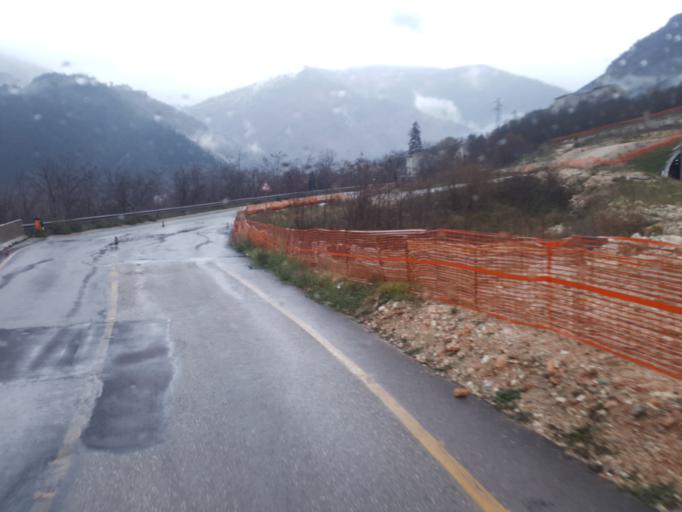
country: IT
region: The Marches
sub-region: Provincia di Ancona
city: Genga
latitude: 43.3979
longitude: 12.9815
